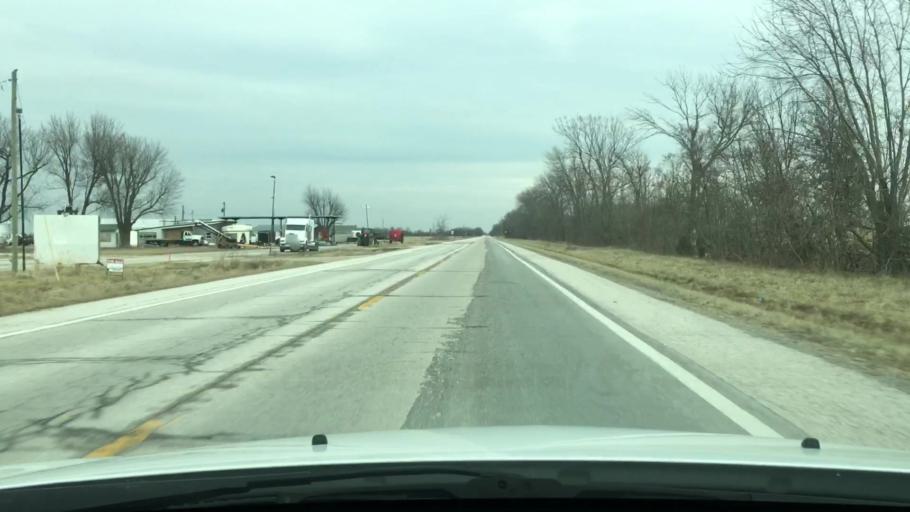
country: US
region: Missouri
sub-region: Audrain County
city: Vandalia
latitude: 39.3185
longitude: -91.4666
